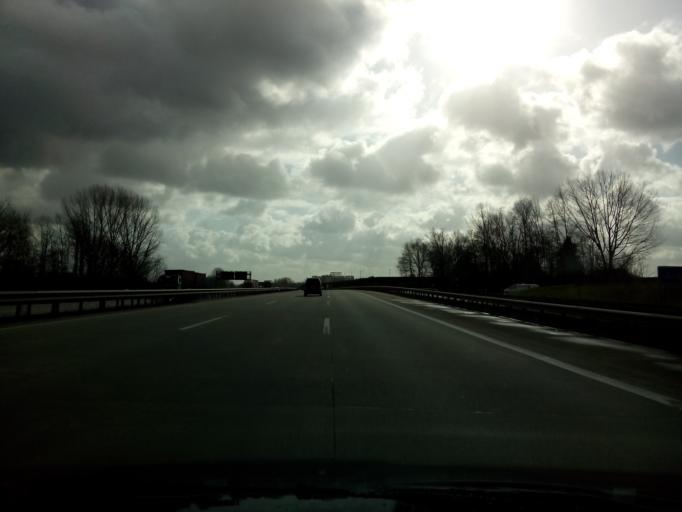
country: DE
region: Lower Saxony
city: Ritterhude
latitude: 53.1425
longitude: 8.7385
